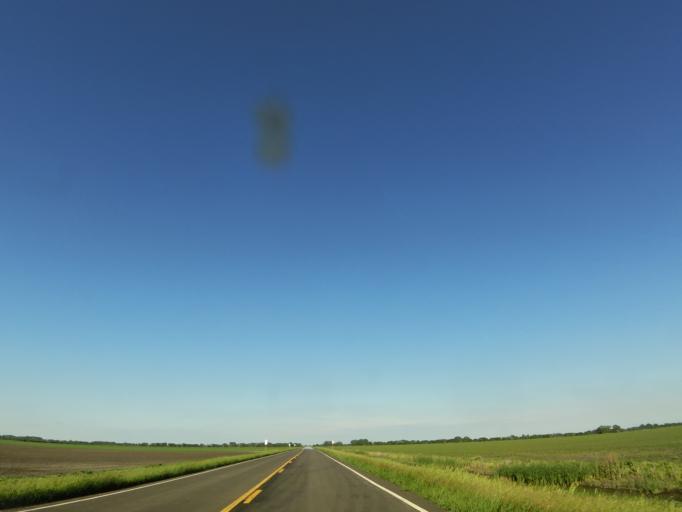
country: US
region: North Dakota
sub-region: Grand Forks County
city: Grand Forks Air Force Base
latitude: 48.1358
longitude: -97.2493
